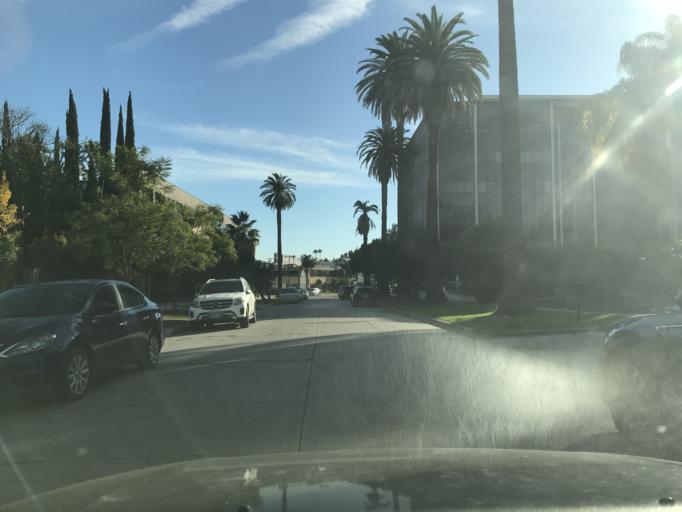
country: US
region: California
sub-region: Los Angeles County
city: Hollywood
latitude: 34.0630
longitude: -118.3214
